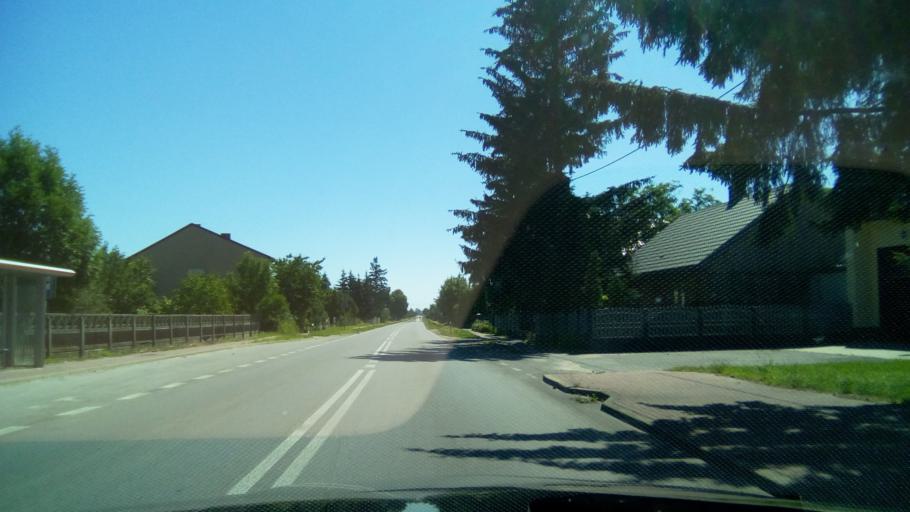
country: PL
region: Masovian Voivodeship
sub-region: Powiat przysuski
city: Potworow
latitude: 51.5080
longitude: 20.7234
